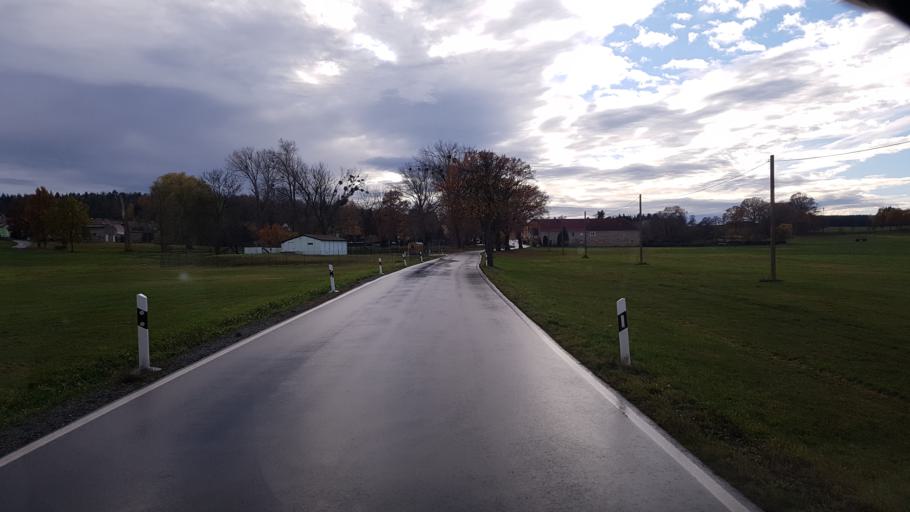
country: DE
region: Brandenburg
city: Grosskmehlen
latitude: 51.3465
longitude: 13.7372
